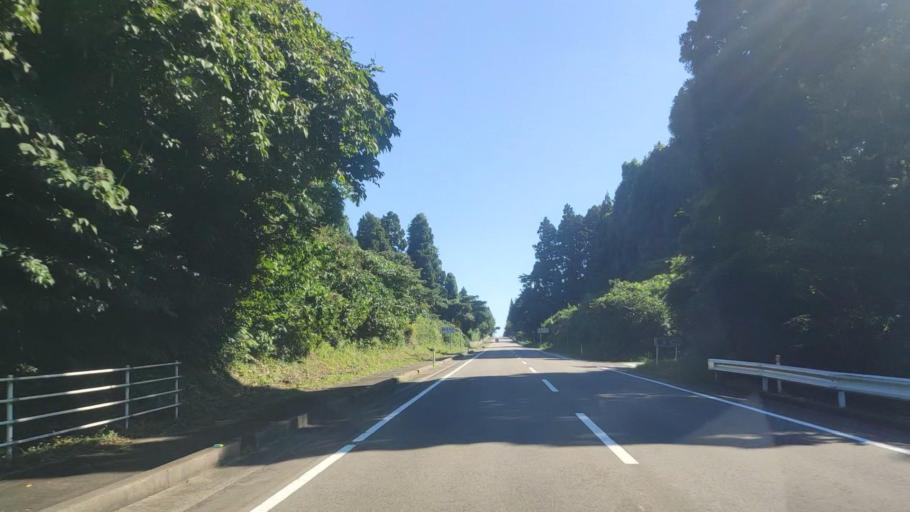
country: JP
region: Ishikawa
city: Nanao
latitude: 37.3740
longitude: 137.2347
